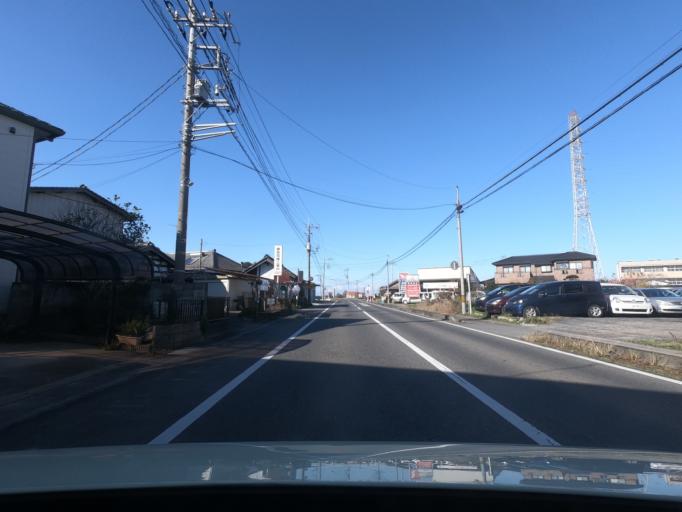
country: JP
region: Ibaraki
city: Ishige
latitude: 36.1727
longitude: 139.9875
